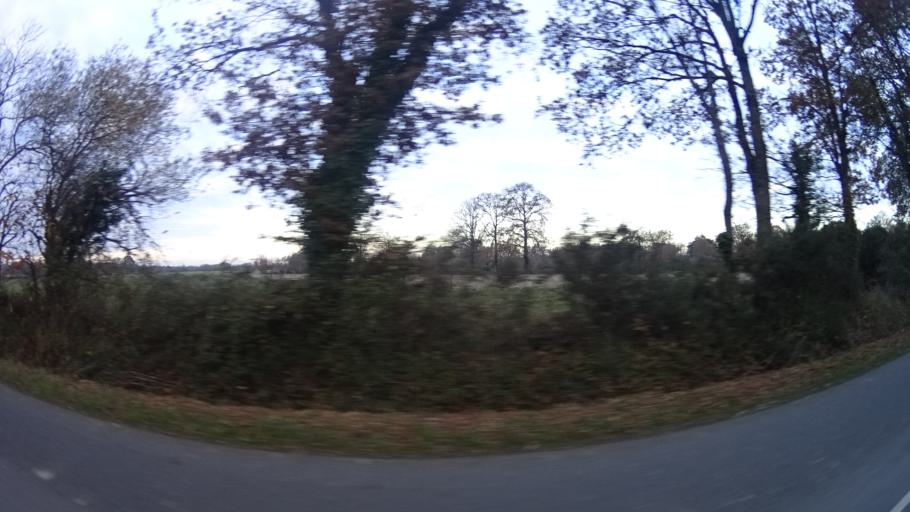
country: FR
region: Brittany
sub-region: Departement d'Ille-et-Vilaine
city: Langon
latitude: 47.6821
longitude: -1.8816
